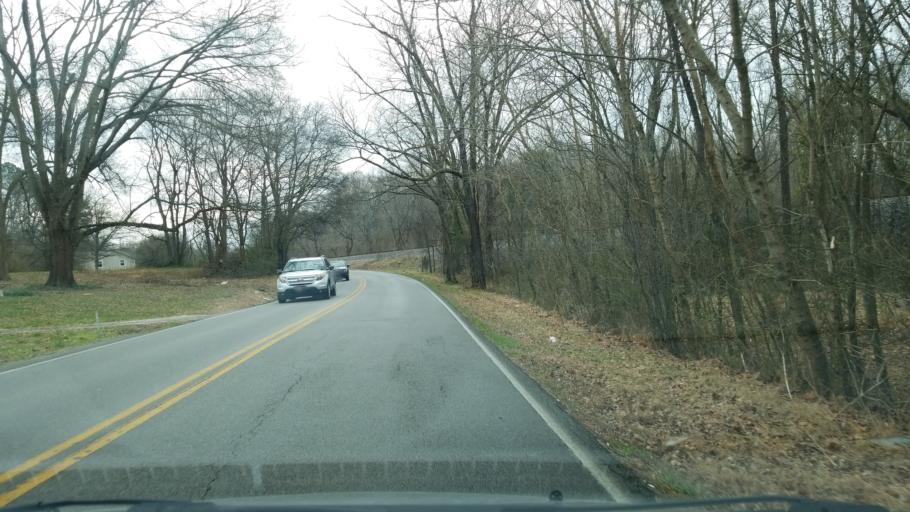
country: US
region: Tennessee
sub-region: Hamilton County
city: East Brainerd
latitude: 34.9812
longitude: -85.1465
